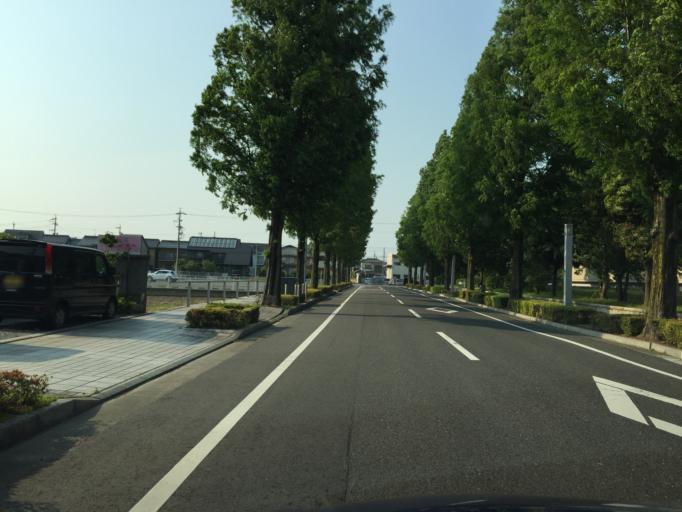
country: JP
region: Gifu
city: Ogaki
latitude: 35.3687
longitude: 136.6381
